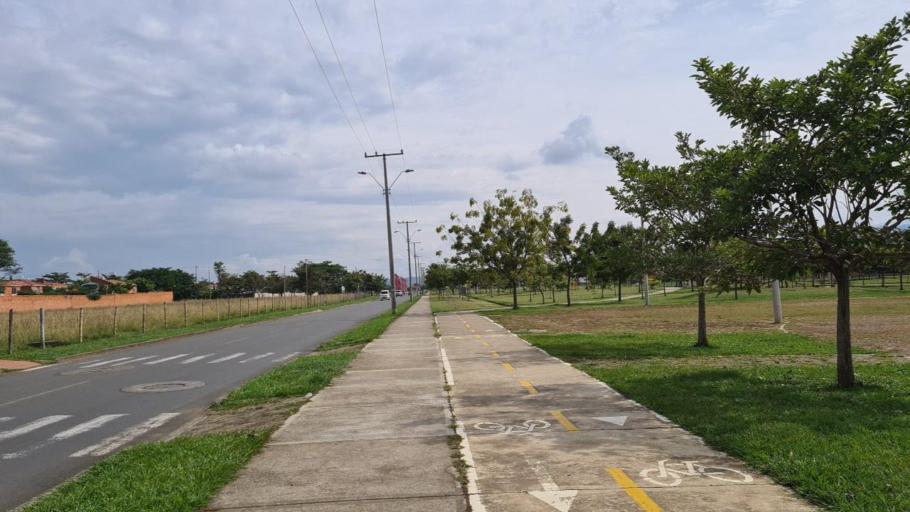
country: CO
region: Valle del Cauca
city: Jamundi
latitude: 3.2572
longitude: -76.5630
